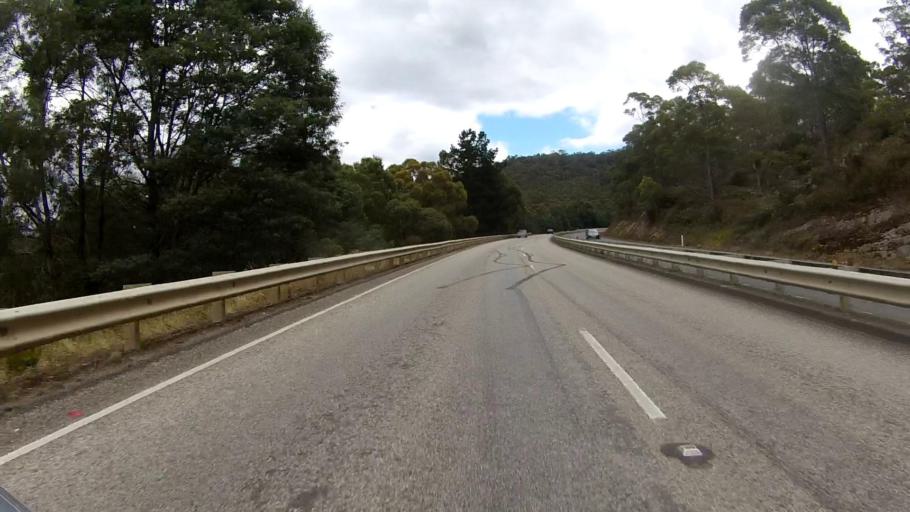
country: AU
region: Tasmania
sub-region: Kingborough
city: Margate
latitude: -42.9859
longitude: 147.1879
